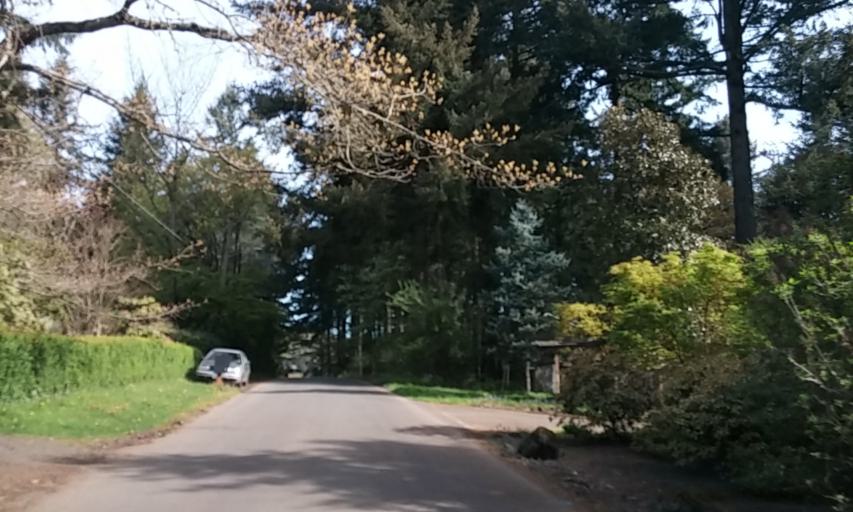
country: US
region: Oregon
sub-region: Washington County
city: West Slope
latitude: 45.5035
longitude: -122.7570
